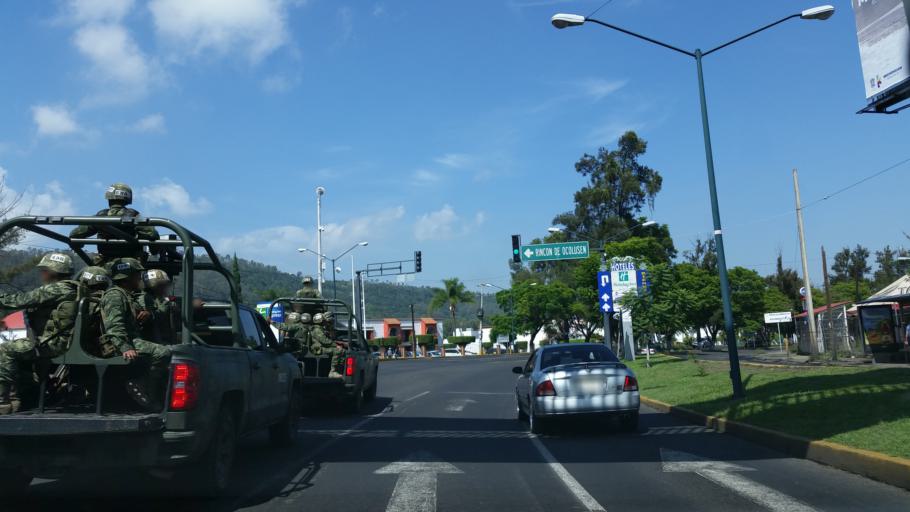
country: MX
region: Michoacan
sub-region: Morelia
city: Puerto de Buenavista (Lazaro Cardenas)
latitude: 19.6876
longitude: -101.1530
